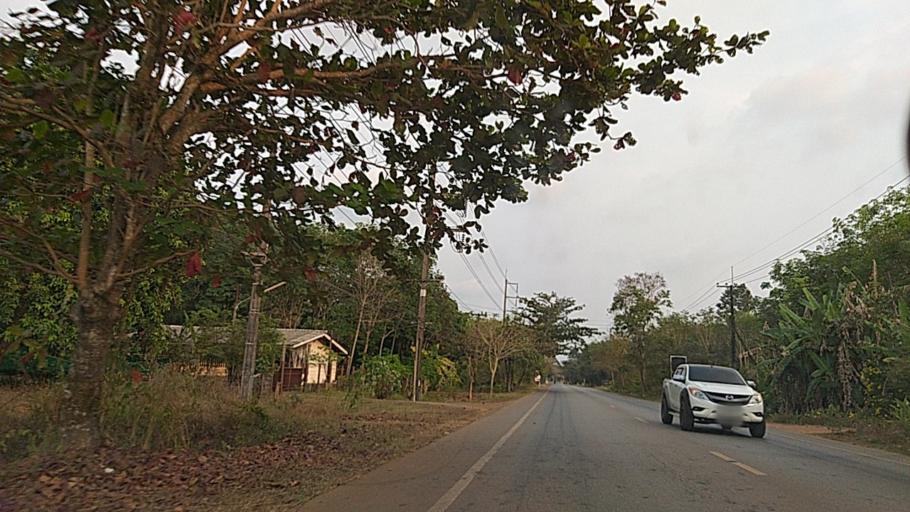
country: TH
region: Trat
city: Laem Ngop
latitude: 12.2367
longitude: 102.2978
